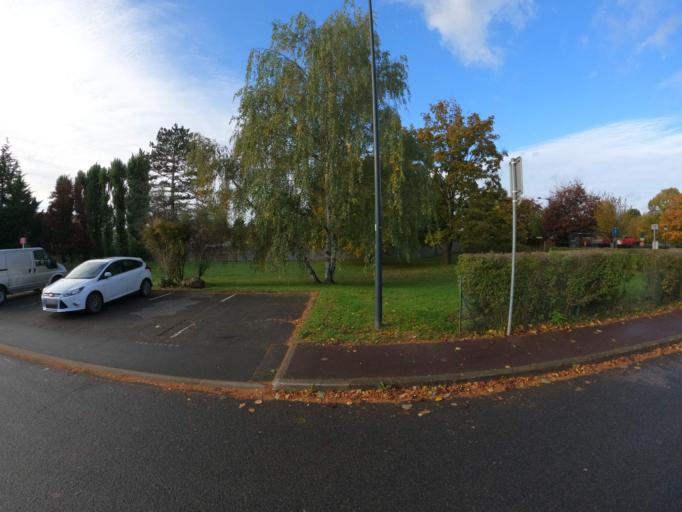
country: FR
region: Ile-de-France
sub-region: Departement de Seine-et-Marne
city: Brou-sur-Chantereine
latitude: 48.8870
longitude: 2.6261
